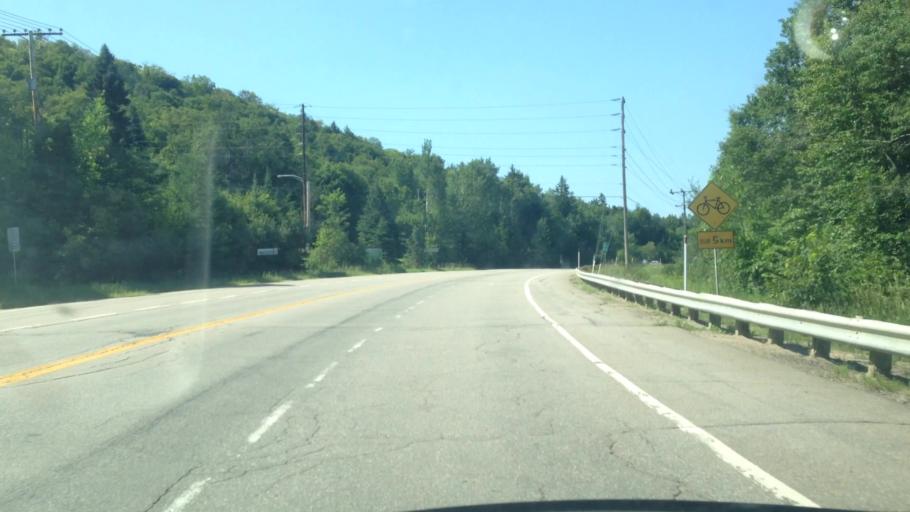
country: CA
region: Quebec
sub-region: Laurentides
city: Mont-Tremblant
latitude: 46.1103
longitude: -74.5973
